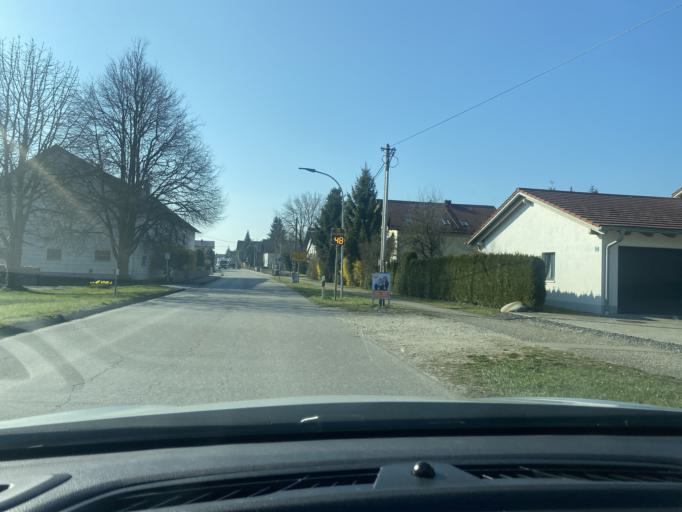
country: DE
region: Bavaria
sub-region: Upper Bavaria
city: Oberding
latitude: 48.3075
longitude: 11.8473
